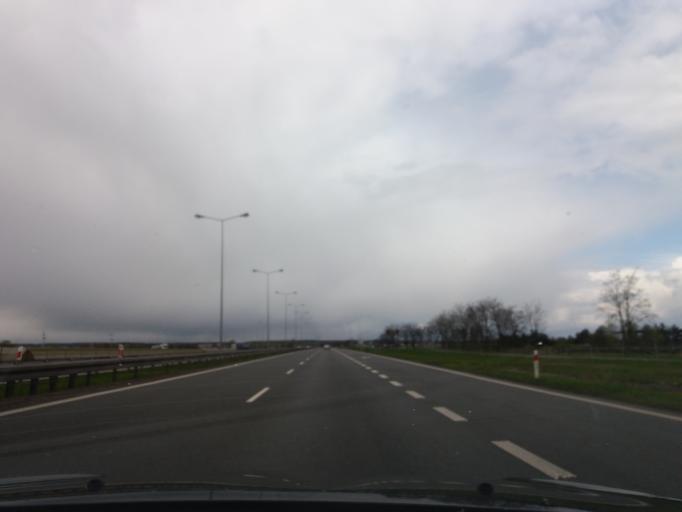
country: PL
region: Opole Voivodeship
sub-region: Powiat opolski
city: Proszkow
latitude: 50.5668
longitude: 17.8650
